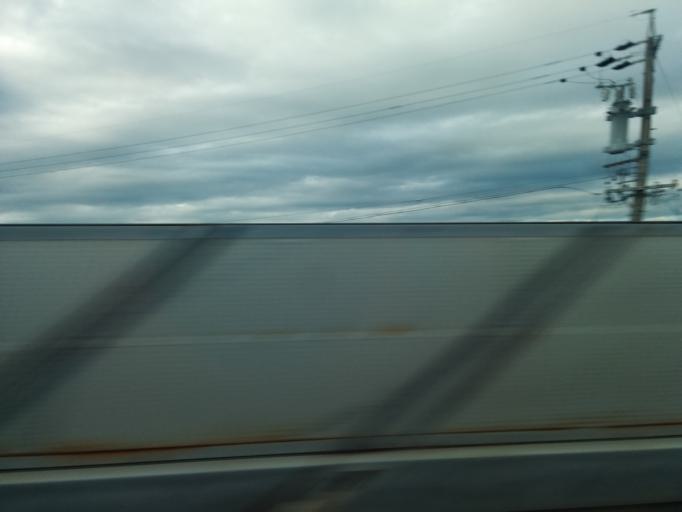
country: JP
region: Shizuoka
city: Fujieda
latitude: 34.8399
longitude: 138.2586
